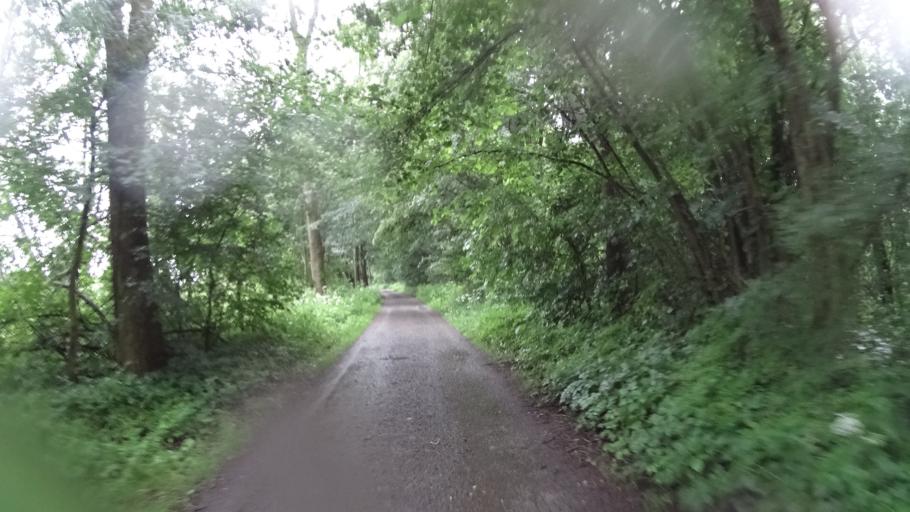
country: AT
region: Upper Austria
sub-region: Politischer Bezirk Scharding
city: Scharding
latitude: 48.4711
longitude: 13.4287
